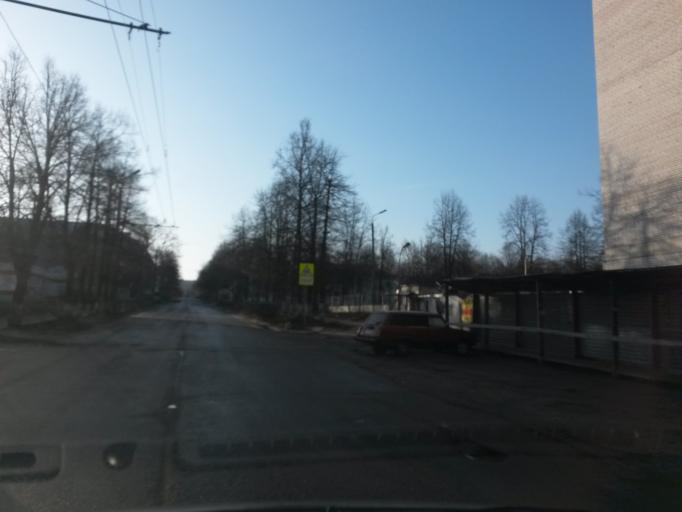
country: RU
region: Jaroslavl
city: Yaroslavl
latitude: 57.5832
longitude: 39.8400
